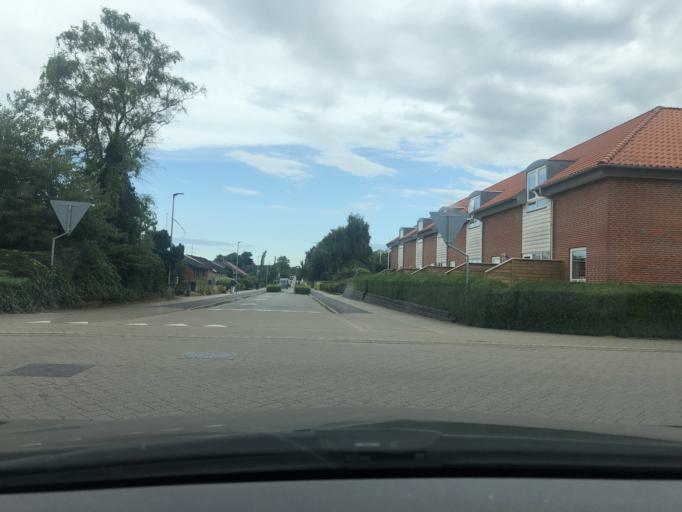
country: DK
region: South Denmark
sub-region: Varde Kommune
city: Olgod
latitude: 55.8073
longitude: 8.6148
